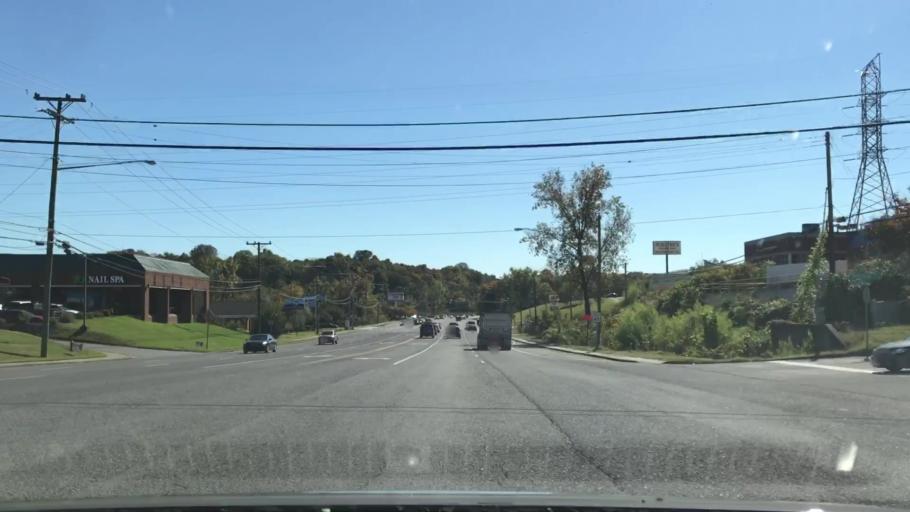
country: US
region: Tennessee
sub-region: Williamson County
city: Brentwood Estates
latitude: 36.0445
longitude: -86.7132
